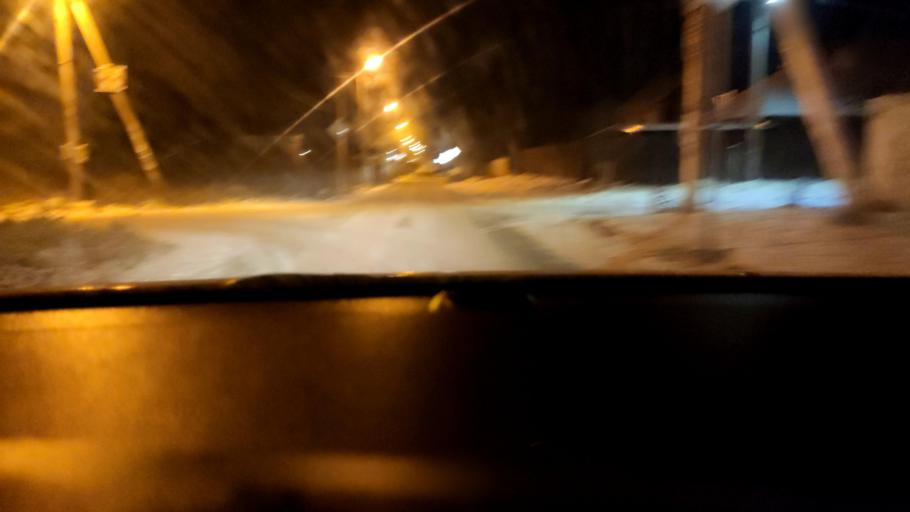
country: RU
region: Tatarstan
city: Osinovo
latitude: 55.8288
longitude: 48.8592
